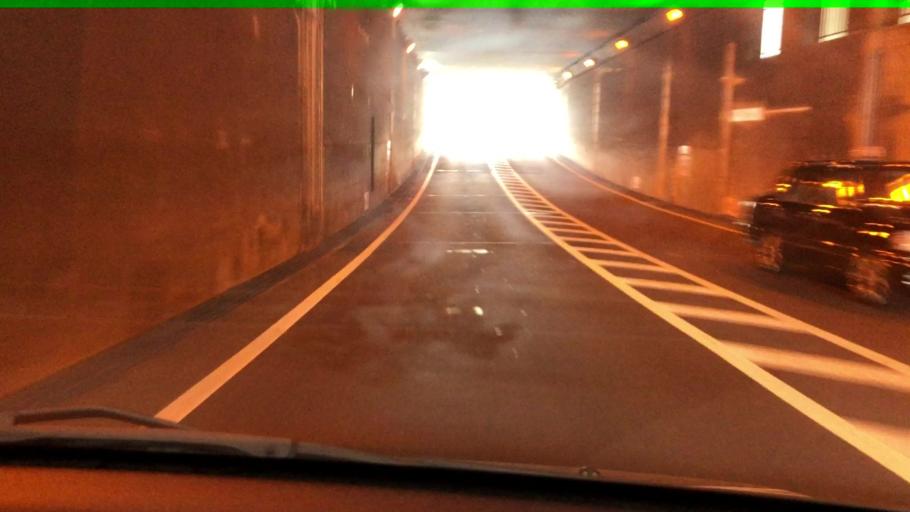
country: JP
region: Hyogo
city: Nishinomiya-hama
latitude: 34.7277
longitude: 135.3562
